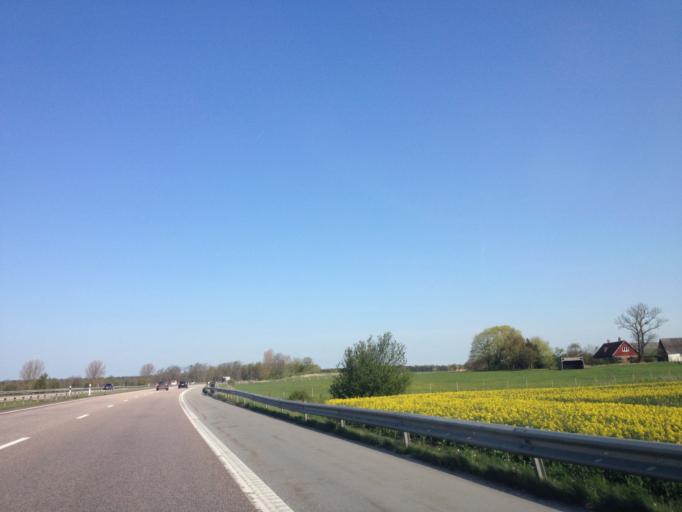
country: SE
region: Skane
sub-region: Kavlinge Kommun
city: Hofterup
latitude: 55.7753
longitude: 12.9736
